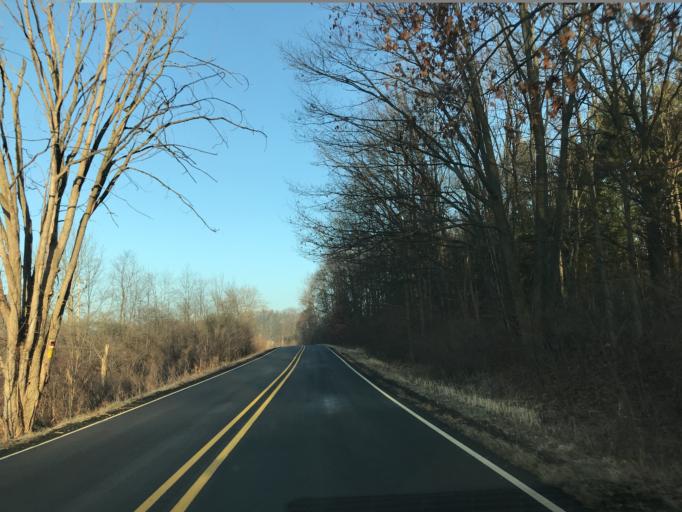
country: US
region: Michigan
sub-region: Ingham County
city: Leslie
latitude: 42.4342
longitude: -84.5366
